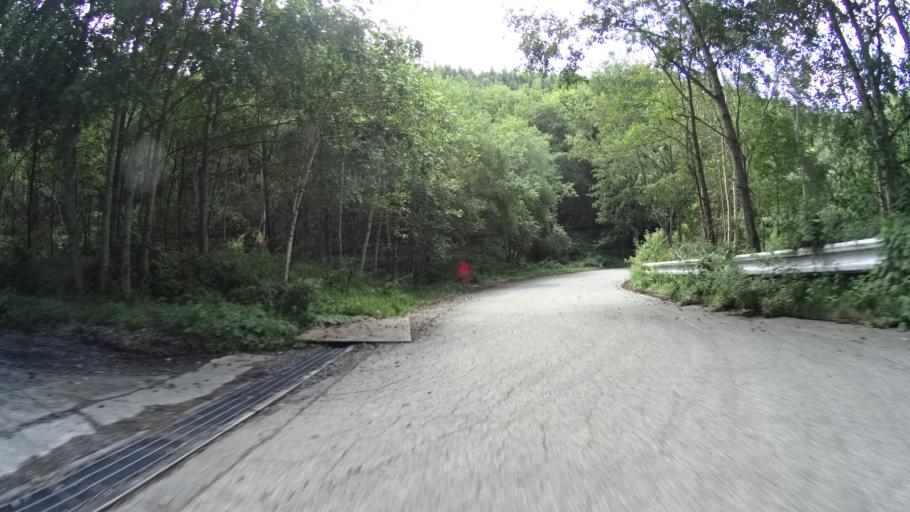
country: JP
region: Yamanashi
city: Enzan
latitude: 35.7176
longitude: 138.8412
